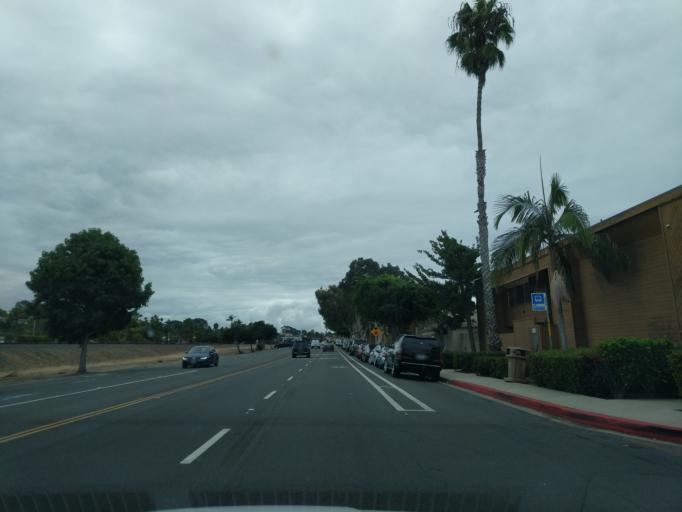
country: US
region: California
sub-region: San Diego County
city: Encinitas
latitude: 33.0566
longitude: -117.2984
